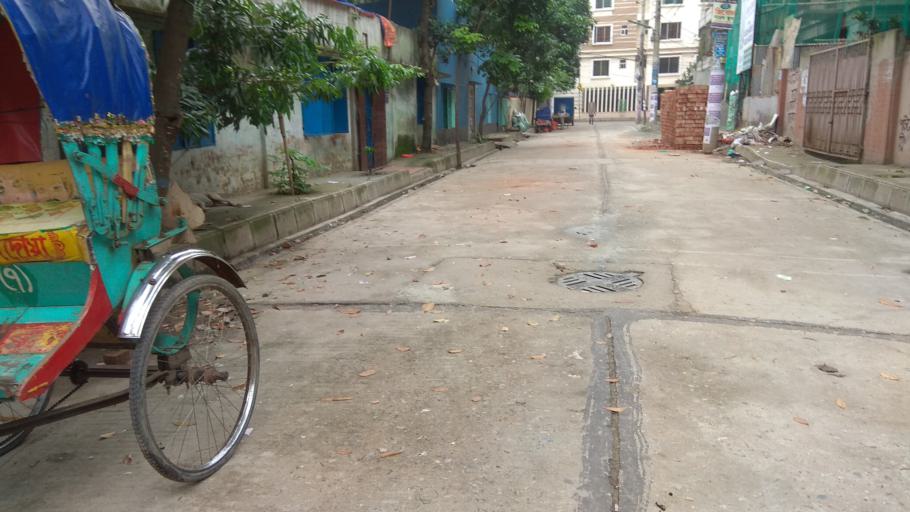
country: BD
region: Dhaka
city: Azimpur
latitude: 23.8058
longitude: 90.3573
